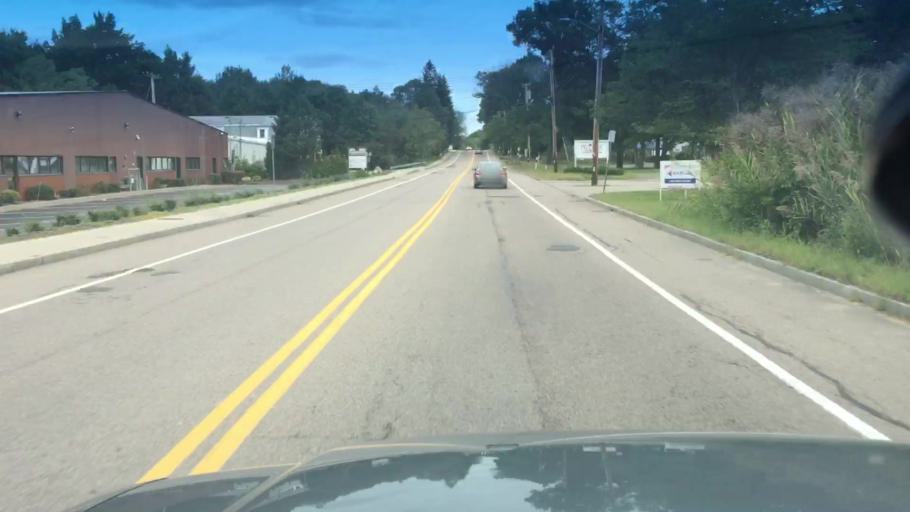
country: US
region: Massachusetts
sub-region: Norfolk County
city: Medway
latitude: 42.1587
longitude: -71.3823
